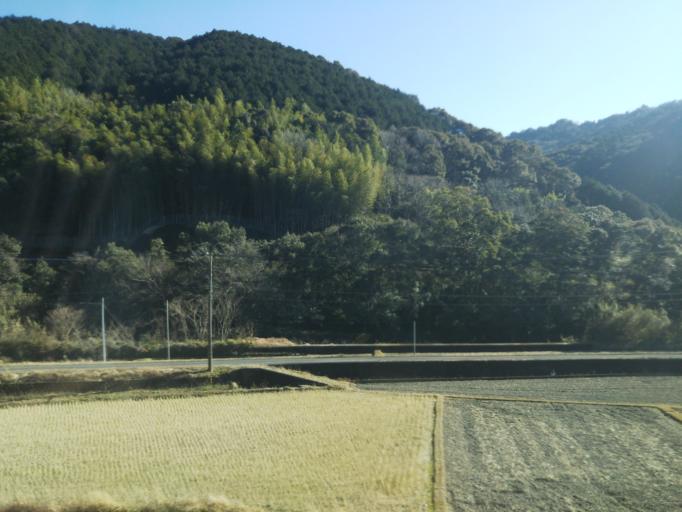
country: JP
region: Kochi
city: Nakamura
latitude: 33.1117
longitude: 133.1106
